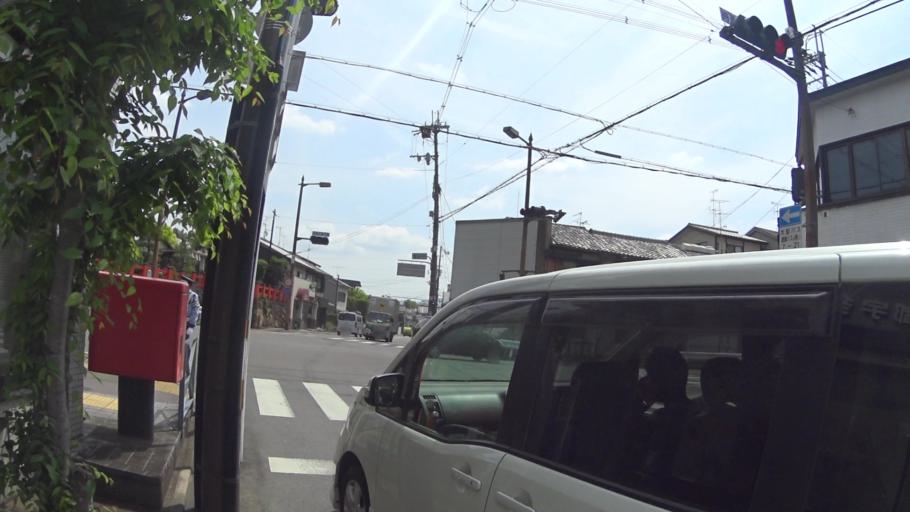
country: JP
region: Kyoto
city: Kyoto
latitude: 35.0288
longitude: 135.7087
